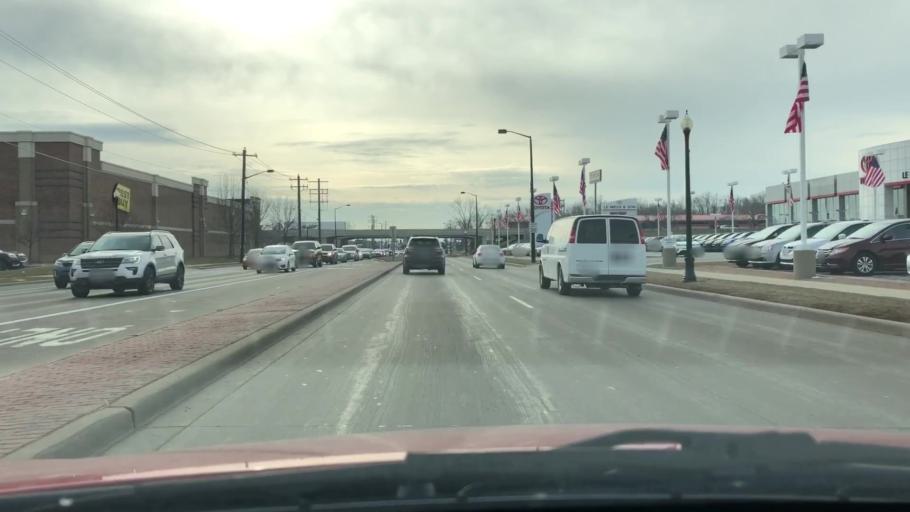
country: US
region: Wisconsin
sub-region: Brown County
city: Ashwaubenon
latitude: 44.4824
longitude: -88.0700
